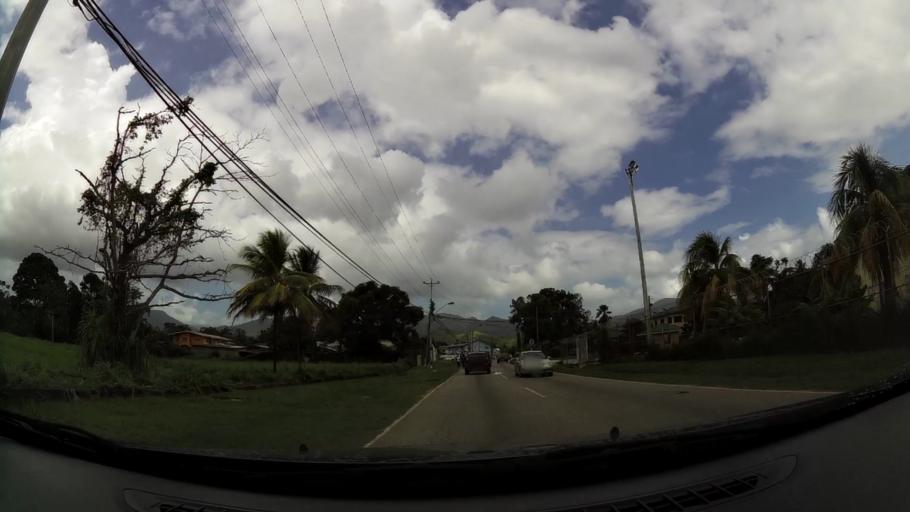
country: TT
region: Tunapuna/Piarco
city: Arouca
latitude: 10.6277
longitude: -61.3391
